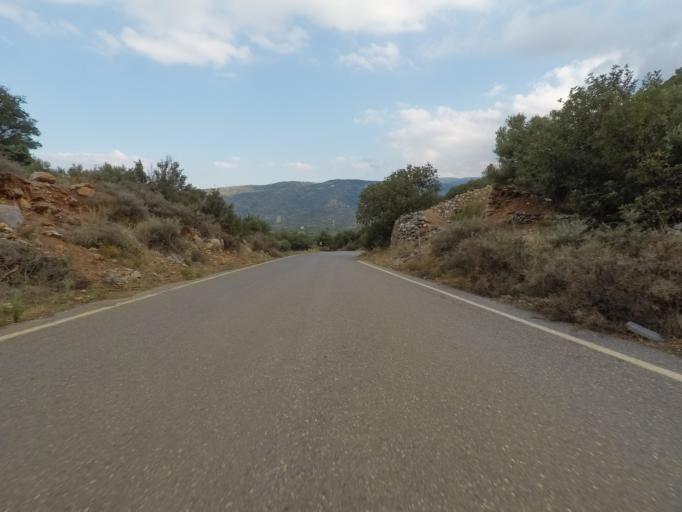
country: GR
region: Crete
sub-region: Nomos Lasithiou
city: Kritsa
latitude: 35.1684
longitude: 25.6547
